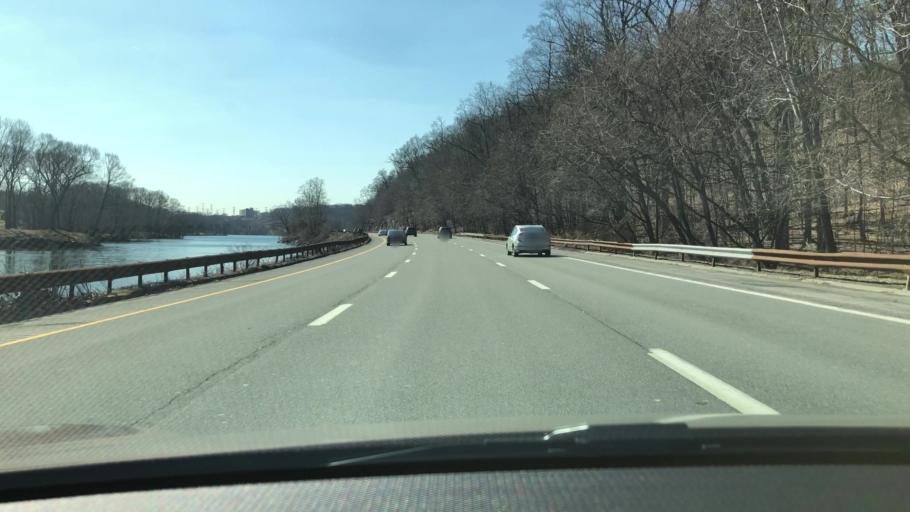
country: US
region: New York
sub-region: Westchester County
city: Ardsley
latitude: 40.9841
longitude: -73.8450
